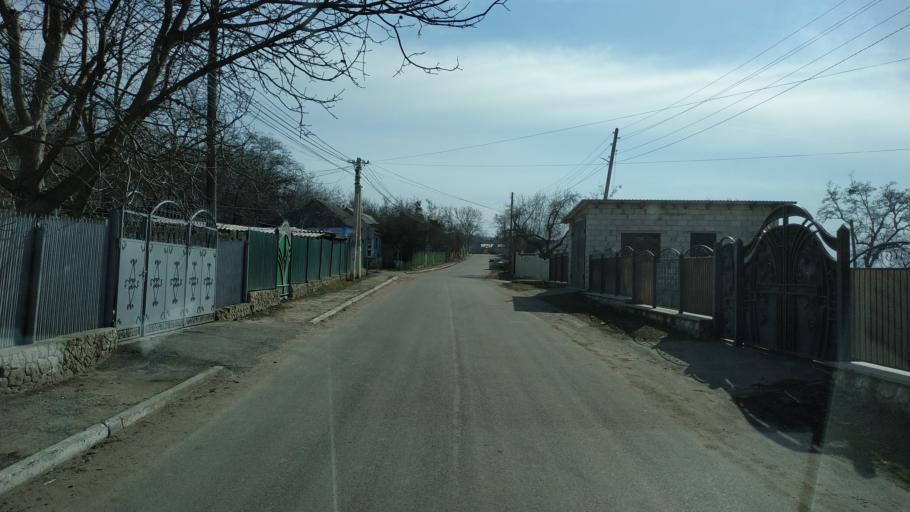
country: MD
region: Nisporeni
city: Nisporeni
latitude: 47.1757
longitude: 28.1261
